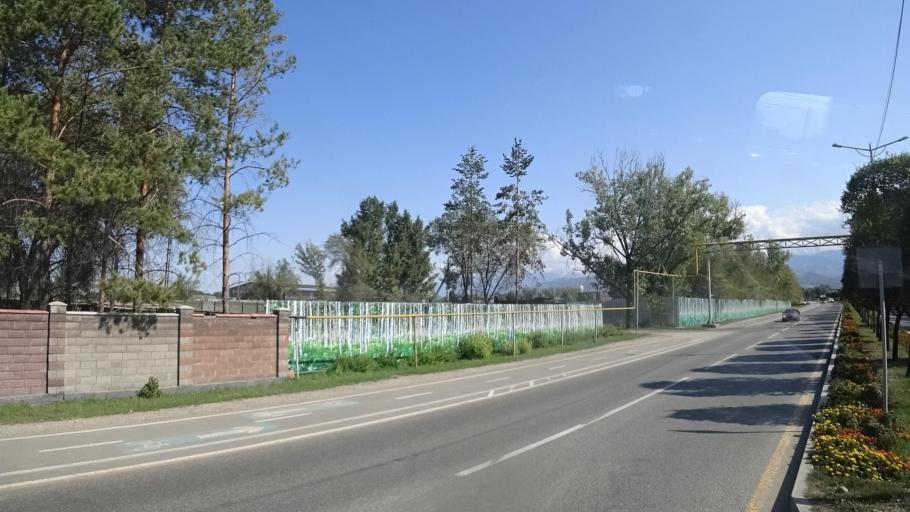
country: KZ
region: Almaty Oblysy
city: Pervomayskiy
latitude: 43.3347
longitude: 77.0038
